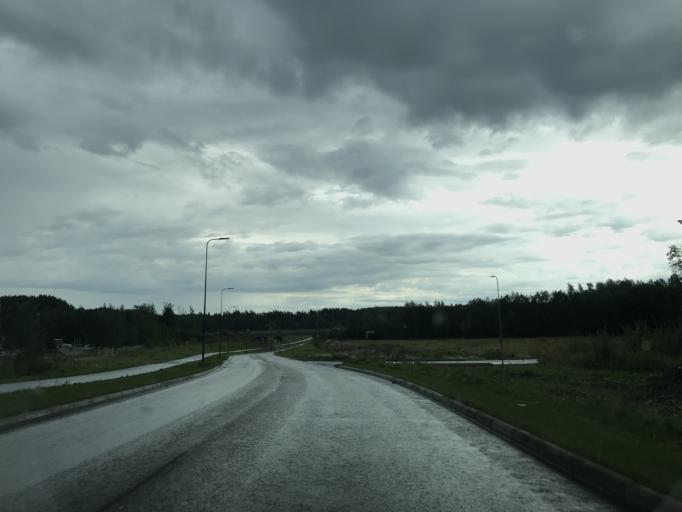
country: FI
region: Uusimaa
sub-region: Helsinki
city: Vihti
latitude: 60.3248
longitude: 24.3042
